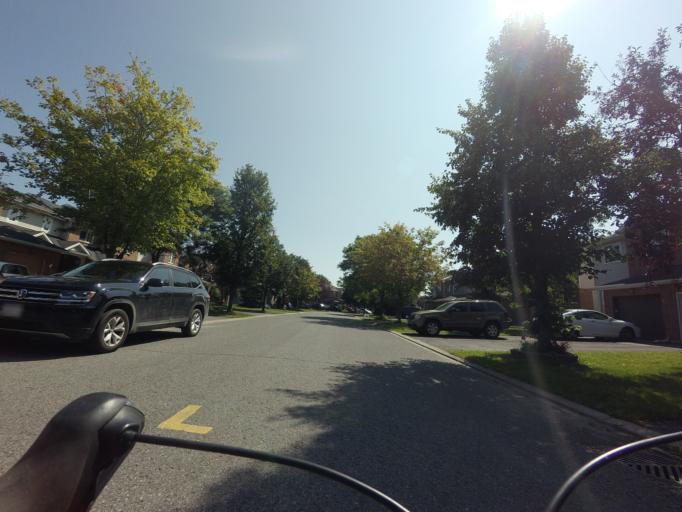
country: CA
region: Ontario
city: Bells Corners
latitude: 45.2805
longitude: -75.8535
